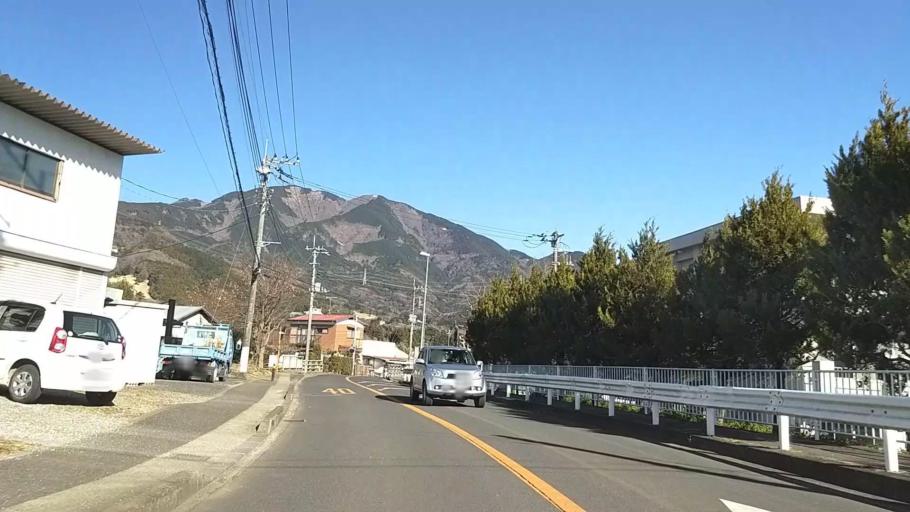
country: JP
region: Kanagawa
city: Hadano
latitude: 35.3999
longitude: 139.1883
